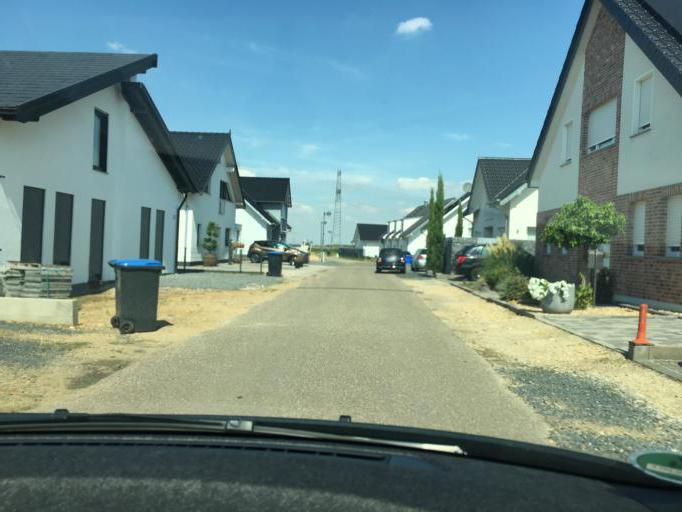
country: DE
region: North Rhine-Westphalia
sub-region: Regierungsbezirk Koln
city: Merzenich
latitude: 50.8416
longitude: 6.5754
